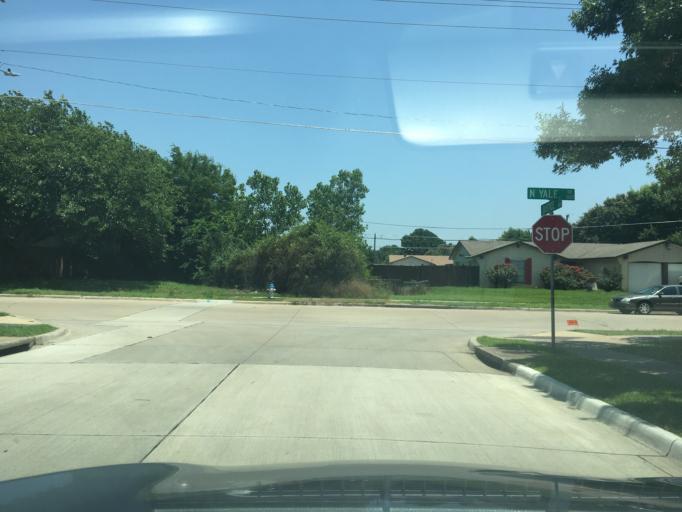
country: US
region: Texas
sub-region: Dallas County
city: Richardson
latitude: 32.9281
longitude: -96.6924
